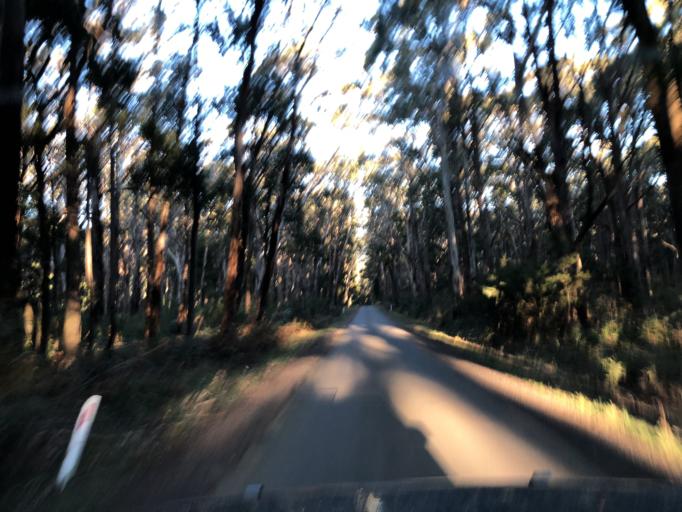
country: AU
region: Victoria
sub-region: Moorabool
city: Bacchus Marsh
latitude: -37.5101
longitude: 144.2088
